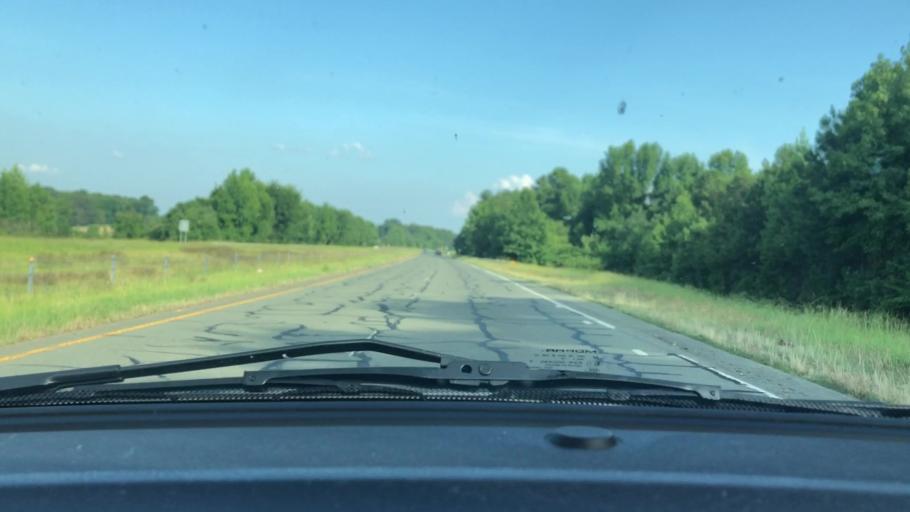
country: US
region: North Carolina
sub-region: Chatham County
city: Siler City
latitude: 35.6889
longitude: -79.4243
